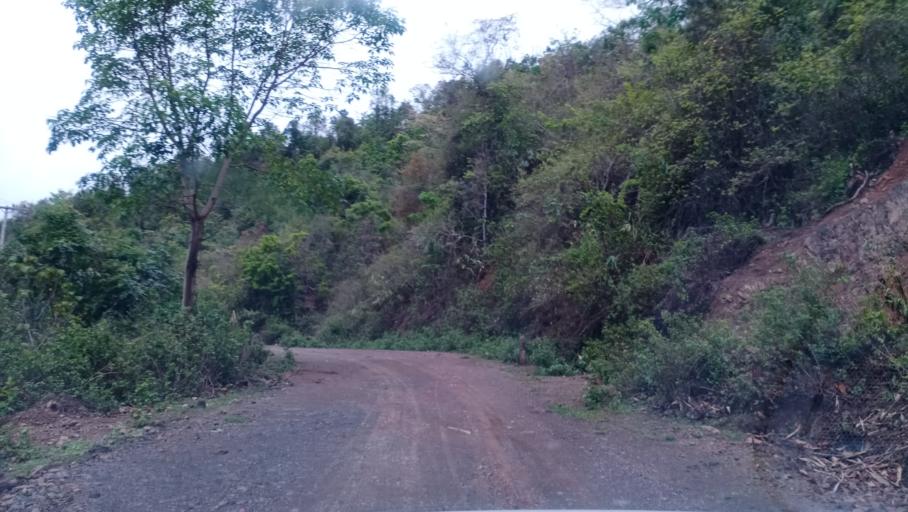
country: LA
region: Phongsali
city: Phongsali
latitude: 21.3482
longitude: 102.0975
